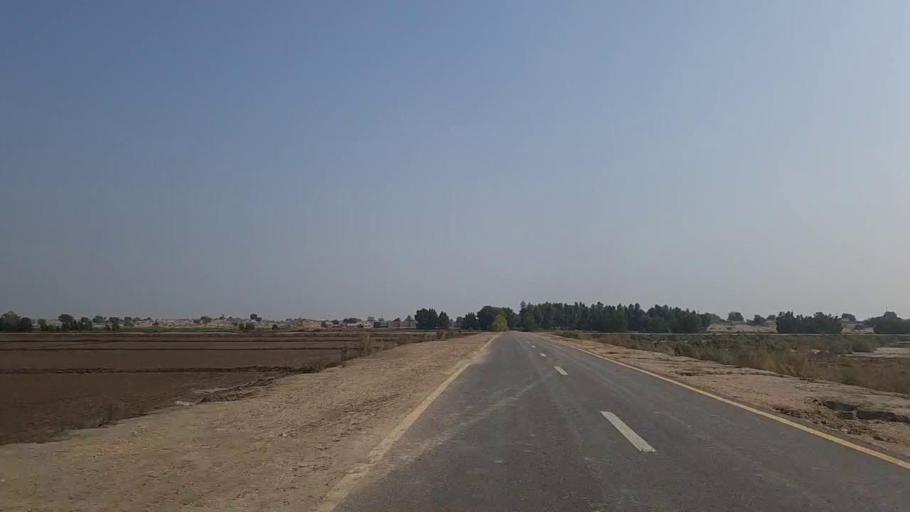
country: PK
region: Sindh
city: Jam Sahib
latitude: 26.3709
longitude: 68.5352
